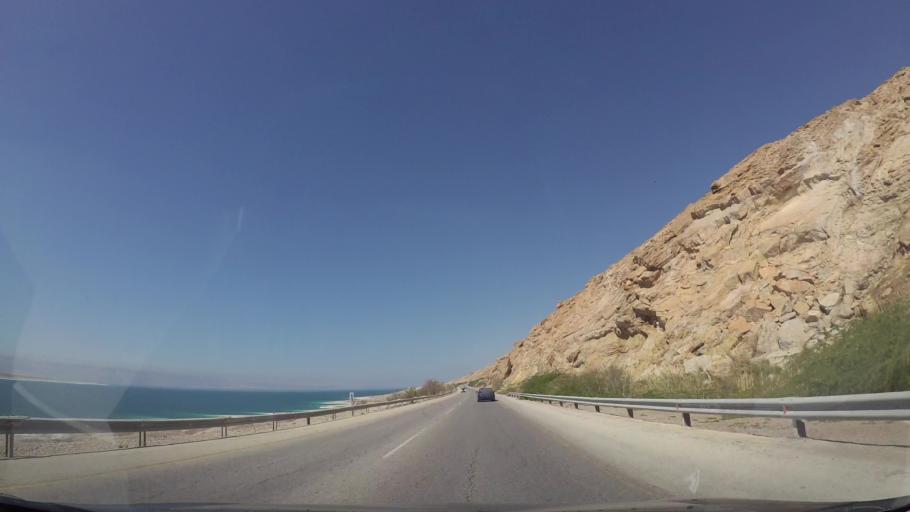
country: JO
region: Karak
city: Al Qasr
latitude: 31.3502
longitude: 35.5480
